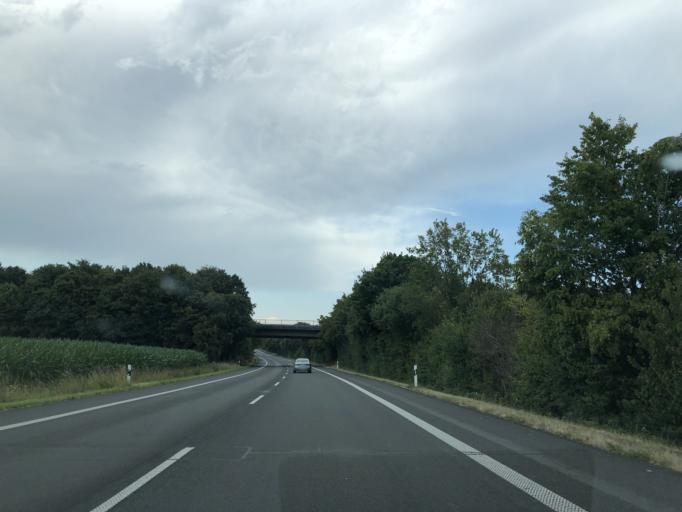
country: DE
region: North Rhine-Westphalia
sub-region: Regierungsbezirk Dusseldorf
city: Kranenburg
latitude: 51.7605
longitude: 6.0368
